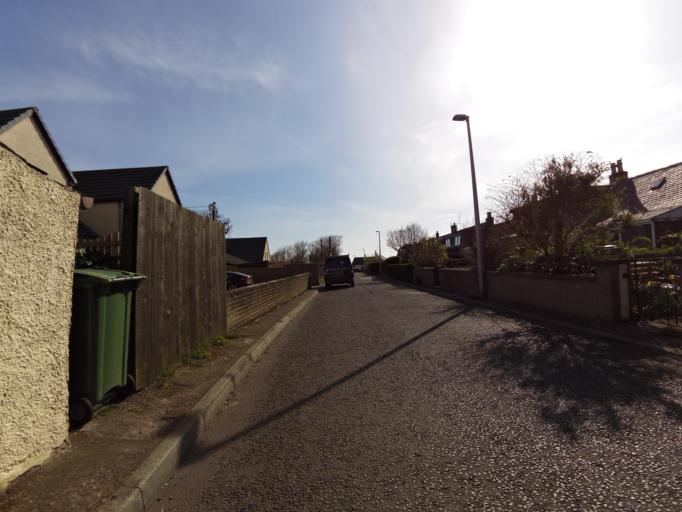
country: GB
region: Scotland
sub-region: Angus
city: Carnoustie
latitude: 56.5028
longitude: -2.6960
